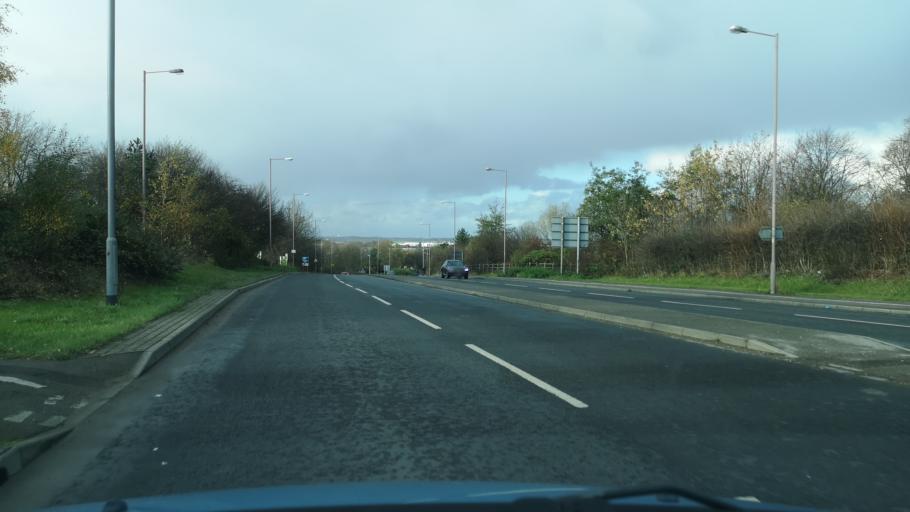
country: GB
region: England
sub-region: City and Borough of Wakefield
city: Normanton
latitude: 53.6996
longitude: -1.3910
